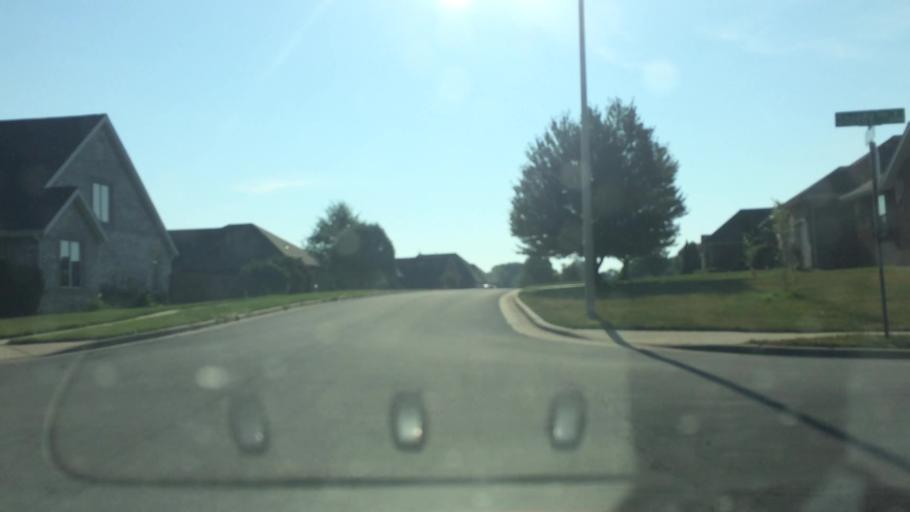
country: US
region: Missouri
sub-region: Greene County
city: Springfield
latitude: 37.2687
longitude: -93.2738
